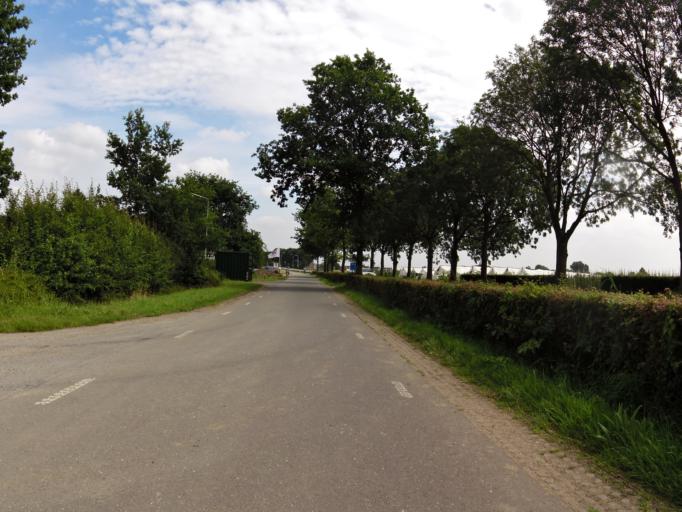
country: NL
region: South Holland
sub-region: Gemeente Leerdam
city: Leerdam
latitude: 51.8810
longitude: 5.1496
